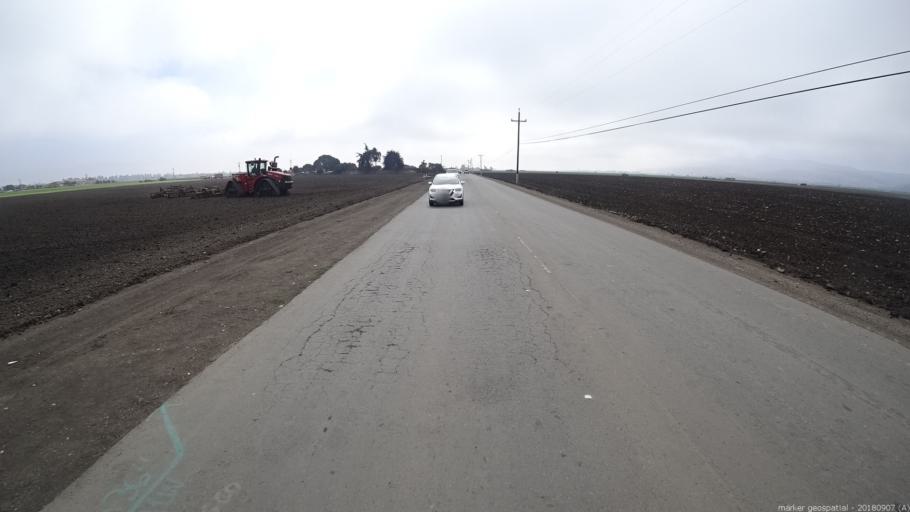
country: US
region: California
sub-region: Monterey County
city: Salinas
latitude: 36.6572
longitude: -121.6890
